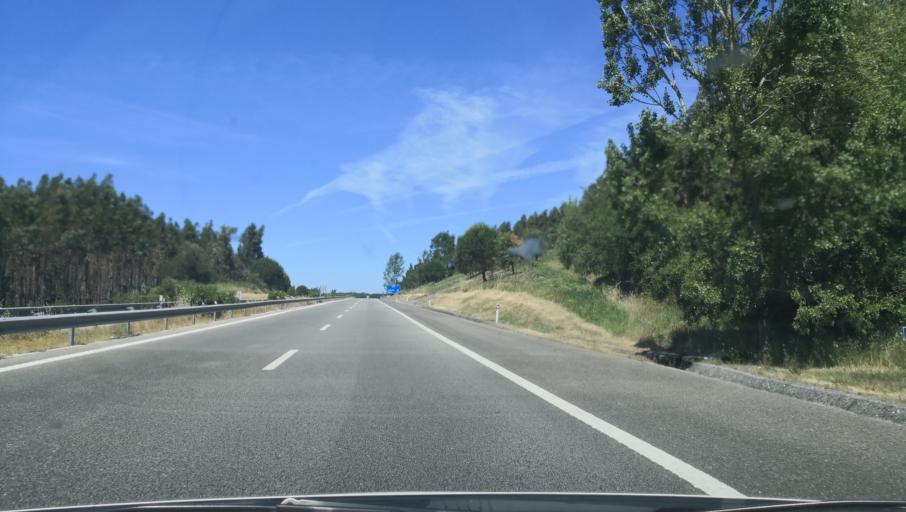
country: PT
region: Coimbra
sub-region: Montemor-O-Velho
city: Montemor-o-Velho
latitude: 40.1778
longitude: -8.7065
